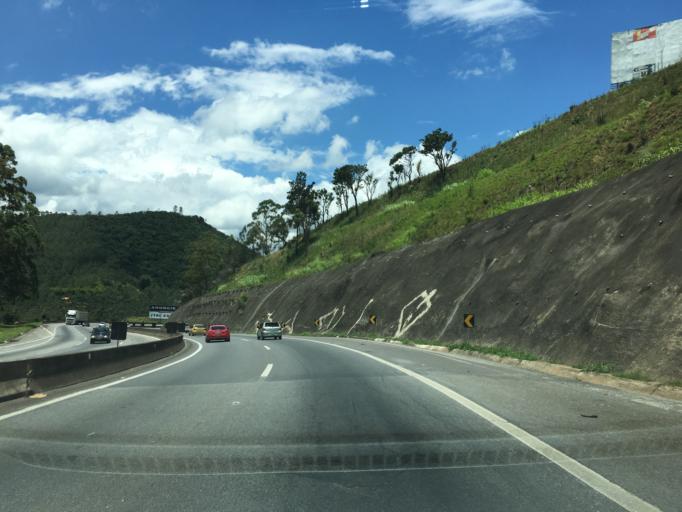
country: BR
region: Sao Paulo
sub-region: Mairipora
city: Mairipora
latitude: -23.2910
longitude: -46.5848
